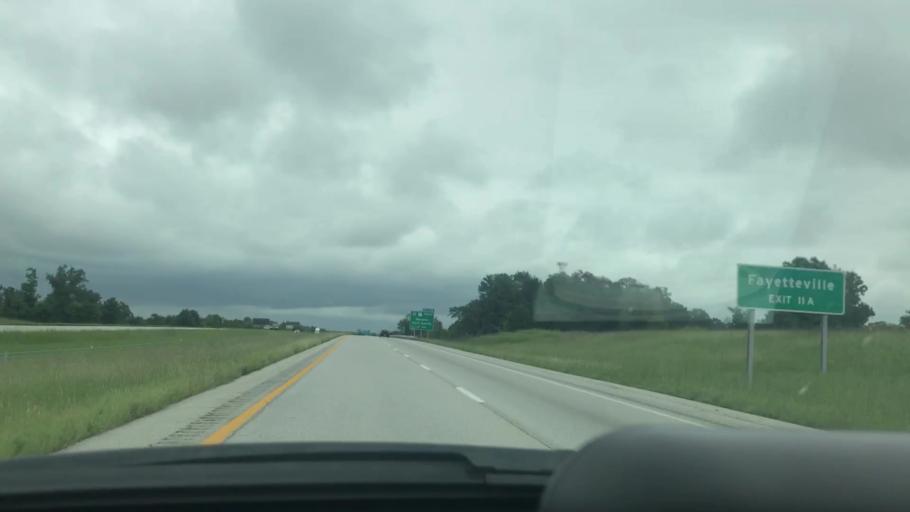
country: US
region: Missouri
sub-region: Jasper County
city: Duquesne
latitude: 37.0555
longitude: -94.4440
